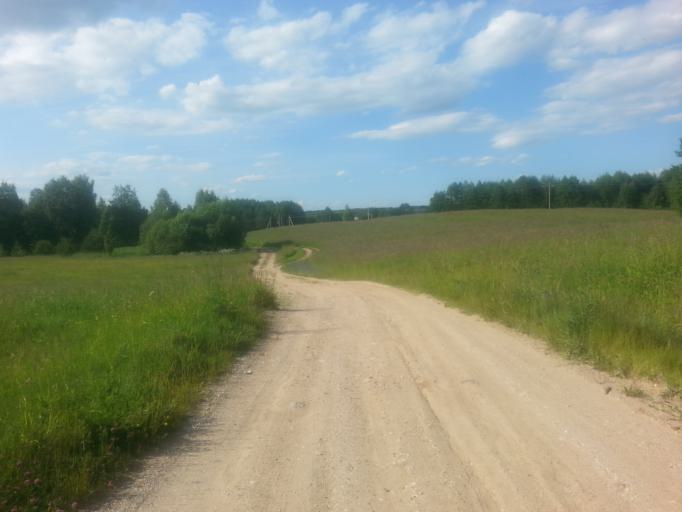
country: BY
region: Minsk
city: Narach
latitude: 54.9725
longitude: 26.6131
